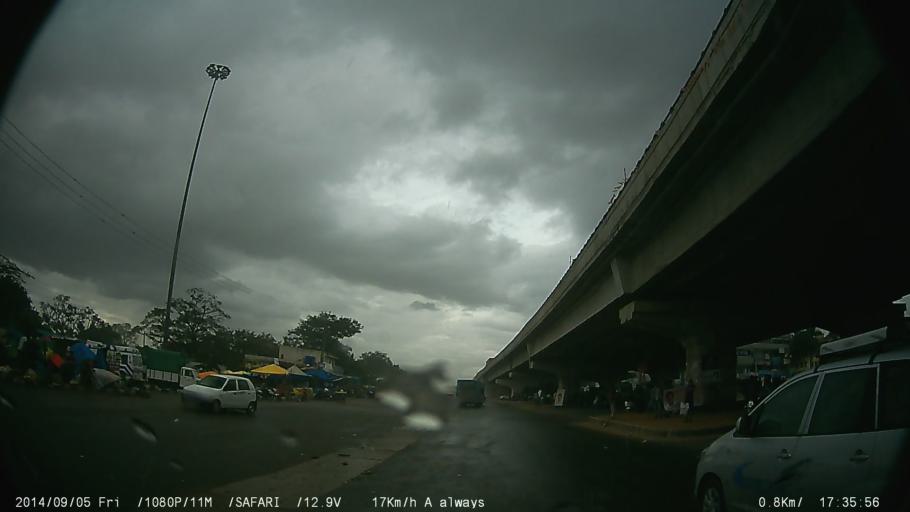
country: IN
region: Karnataka
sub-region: Bangalore Urban
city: Anekal
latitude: 12.8026
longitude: 77.7044
